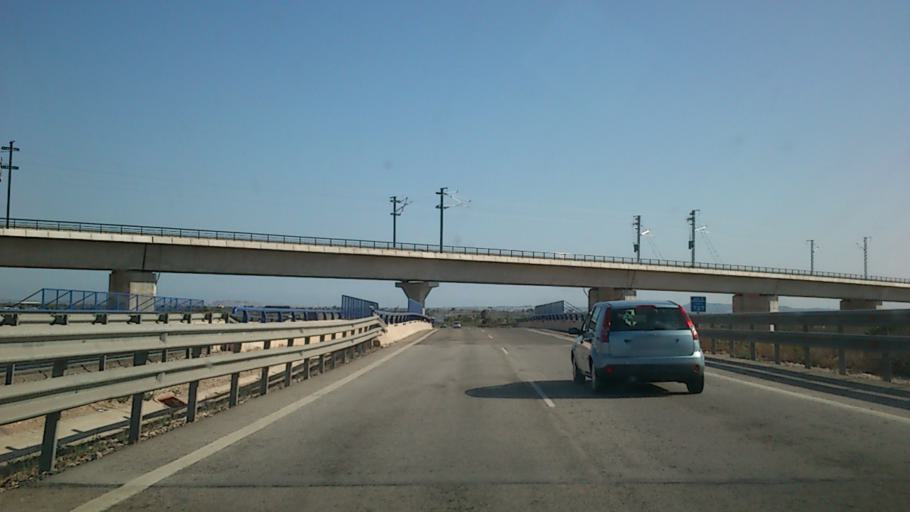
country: ES
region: Valencia
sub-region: Provincia de Alicante
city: San Isidro
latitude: 38.2040
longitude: -0.8167
